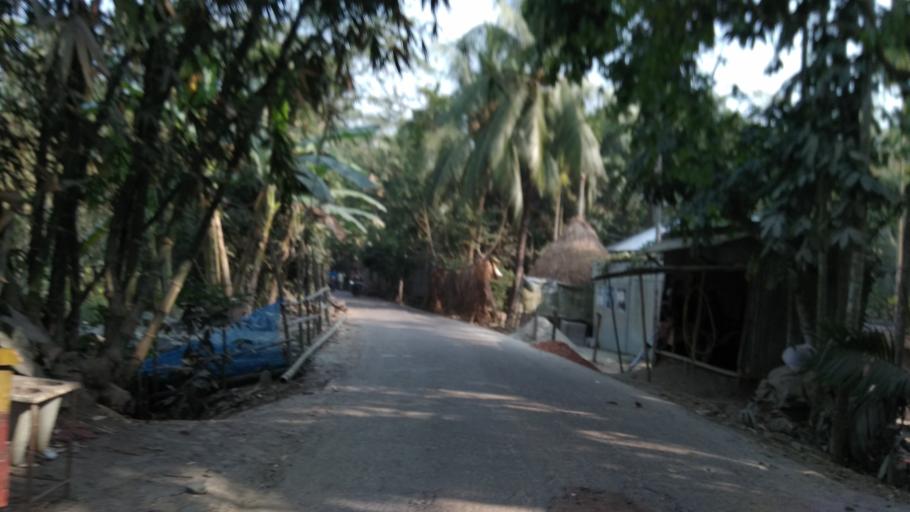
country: BD
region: Barisal
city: Mehendiganj
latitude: 22.9744
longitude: 90.4162
